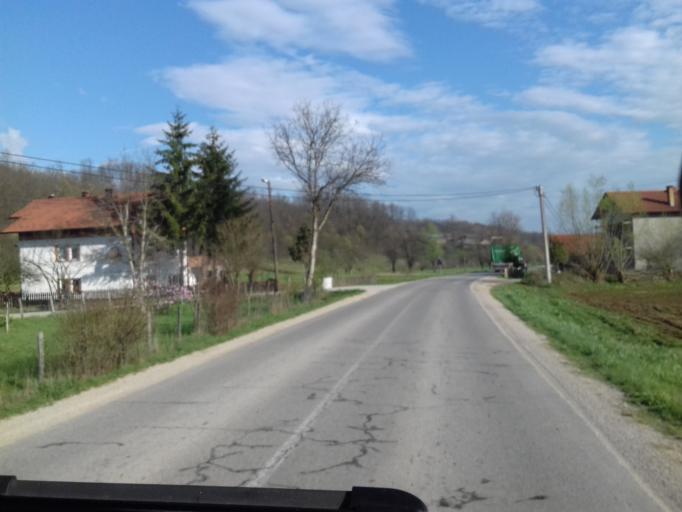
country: BA
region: Federation of Bosnia and Herzegovina
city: Tesanjka
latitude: 44.6511
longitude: 18.0169
